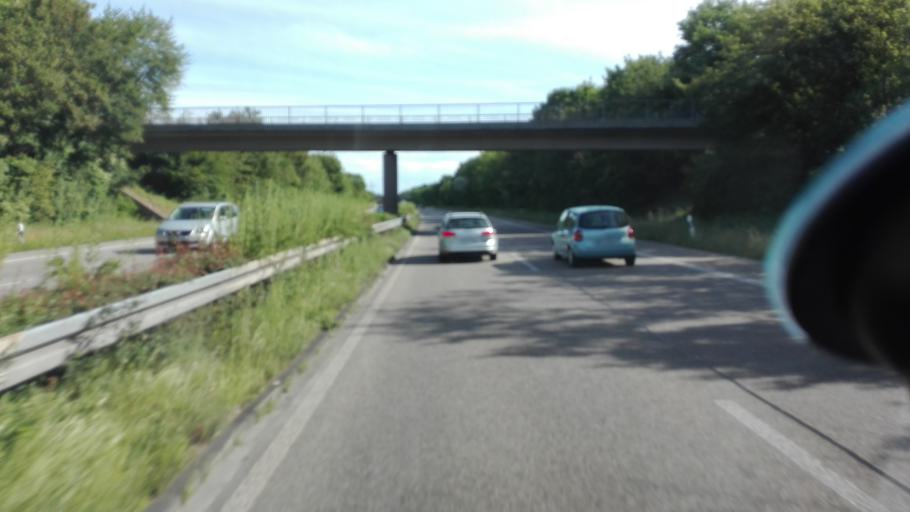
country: DE
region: Baden-Wuerttemberg
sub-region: Karlsruhe Region
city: Eggenstein-Leopoldshafen
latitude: 49.0732
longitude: 8.4070
